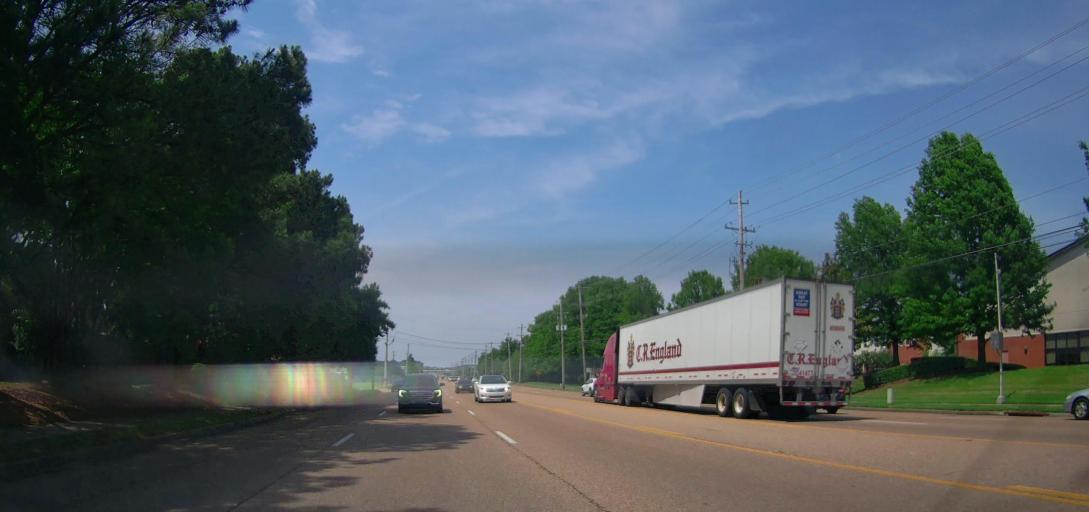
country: US
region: Tennessee
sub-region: Shelby County
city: Germantown
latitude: 35.0294
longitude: -89.7958
